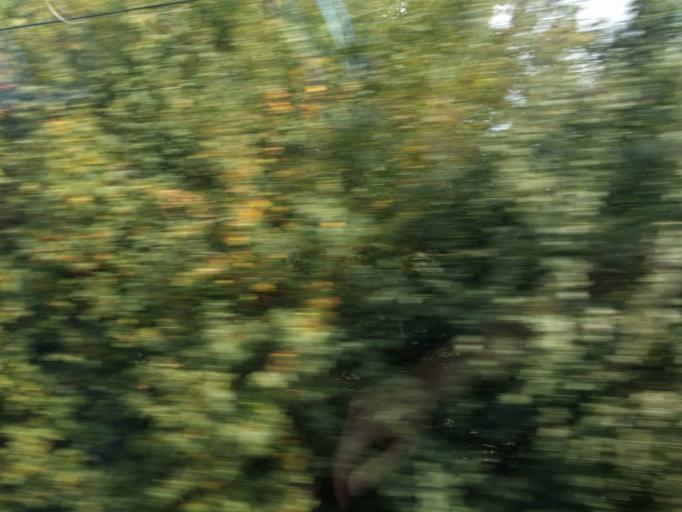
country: DE
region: Schleswig-Holstein
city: Ahrensburg
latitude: 53.6763
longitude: 10.2467
